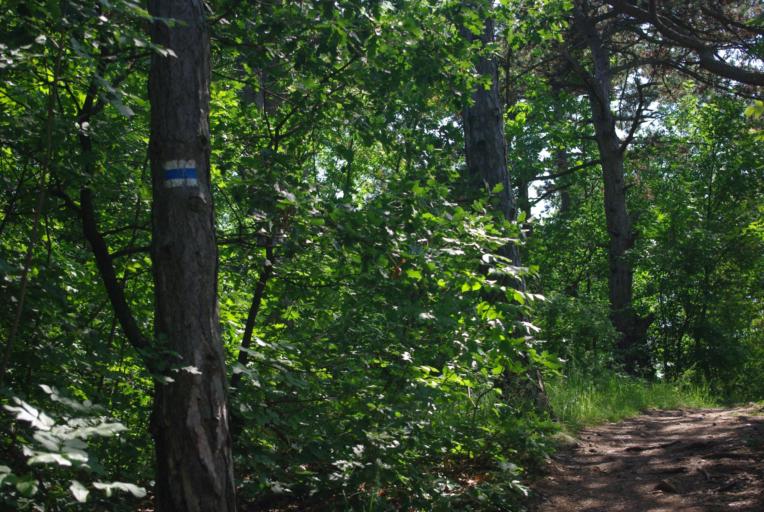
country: HU
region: Pest
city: Pilisborosjeno
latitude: 47.6126
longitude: 18.9791
